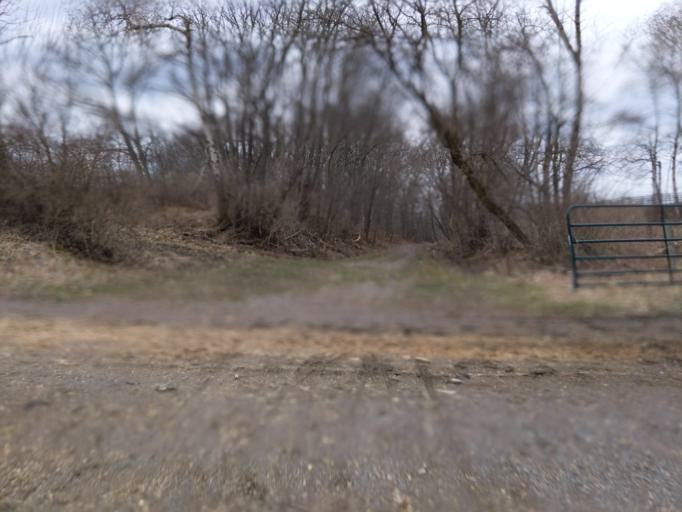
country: US
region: New York
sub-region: Tompkins County
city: Dryden
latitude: 42.5035
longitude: -76.3396
